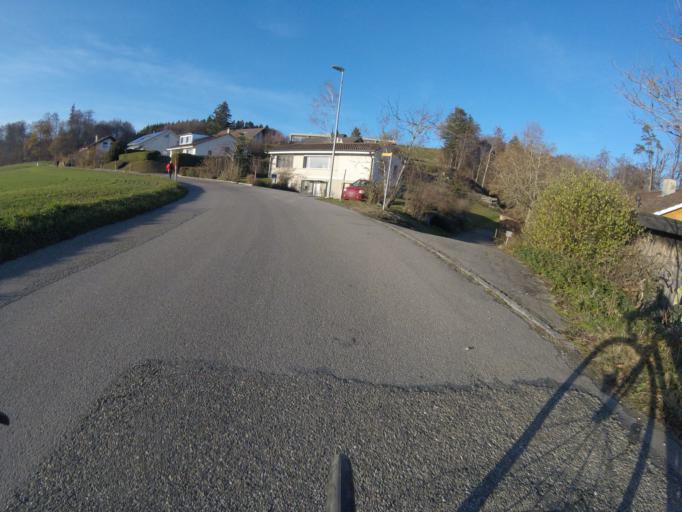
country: CH
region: Bern
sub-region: Bern-Mittelland District
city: Muhleberg
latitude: 46.9388
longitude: 7.2865
